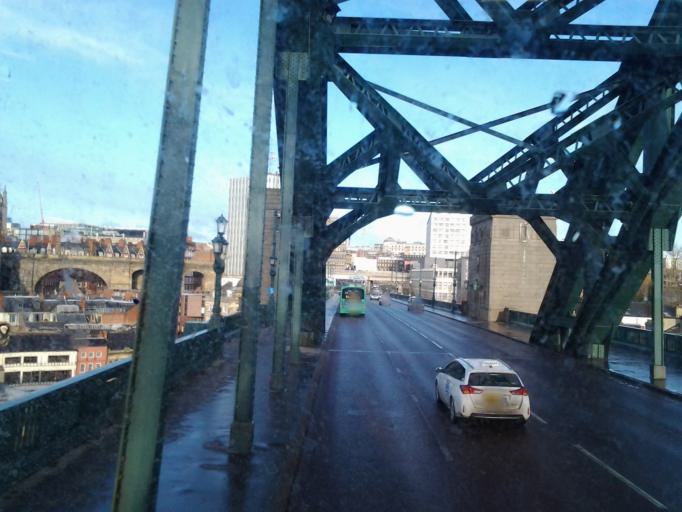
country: GB
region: England
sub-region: Gateshead
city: Gateshead
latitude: 54.9681
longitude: -1.6062
